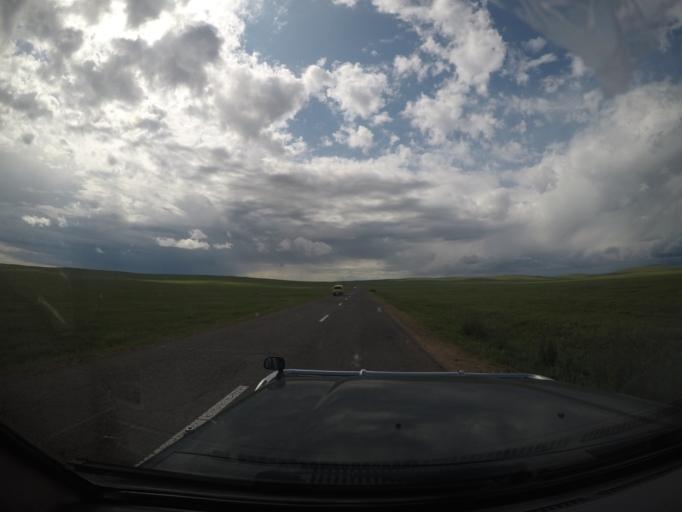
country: MN
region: Hentiy
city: Bayanbulag
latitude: 47.4632
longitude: 109.6164
